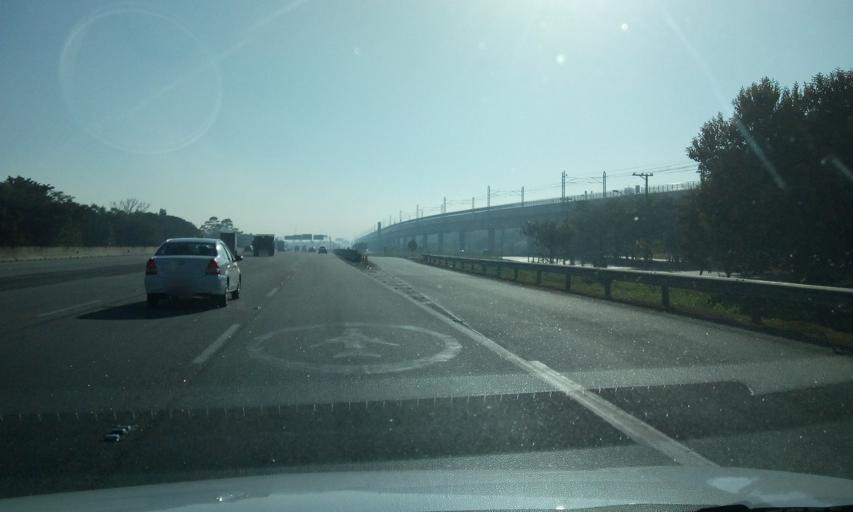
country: BR
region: Sao Paulo
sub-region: Guarulhos
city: Guarulhos
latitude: -23.4856
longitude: -46.5060
